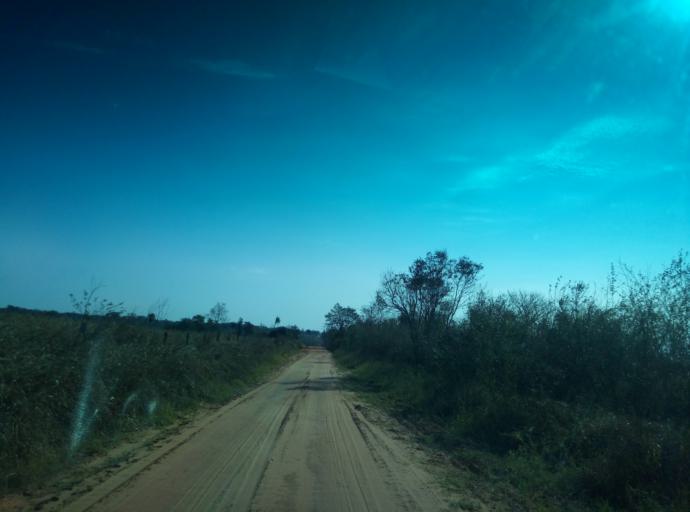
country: PY
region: Caaguazu
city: Doctor Cecilio Baez
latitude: -25.1649
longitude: -56.2185
